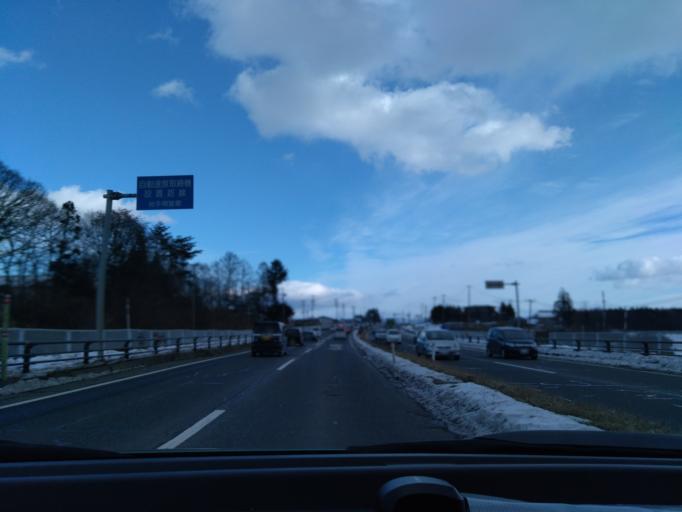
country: JP
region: Iwate
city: Shizukuishi
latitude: 39.7017
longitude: 141.0442
